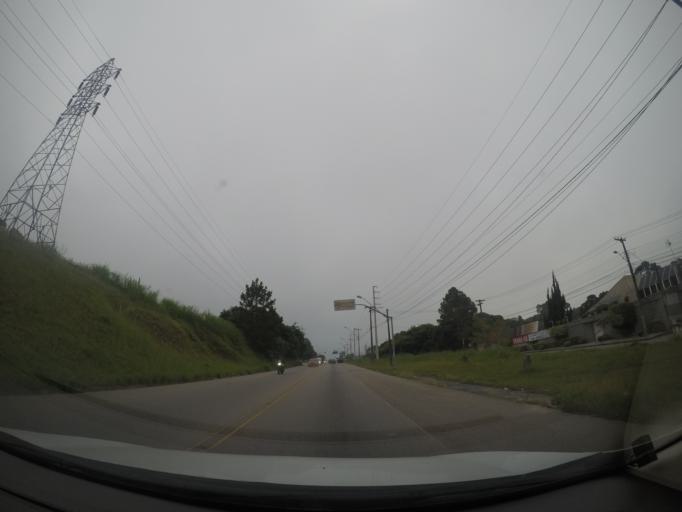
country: BR
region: Parana
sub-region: Curitiba
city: Curitiba
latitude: -25.3773
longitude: -49.2737
